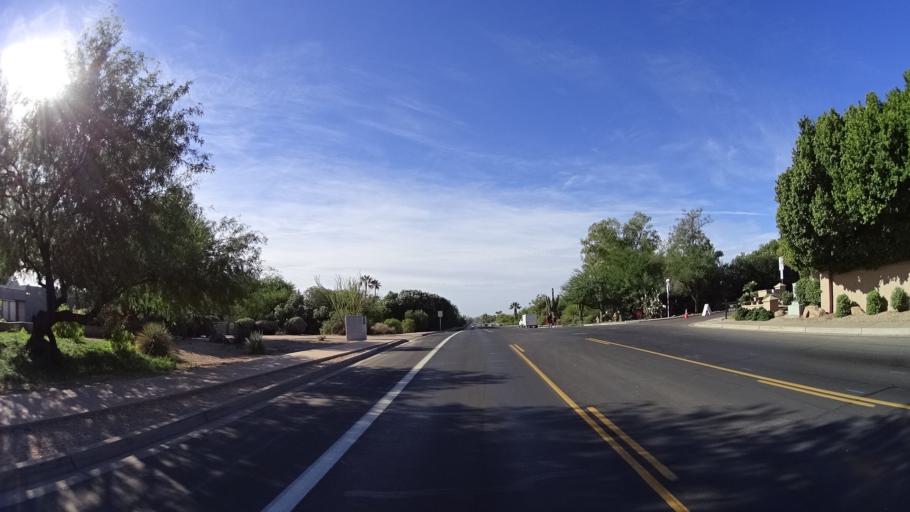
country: US
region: Arizona
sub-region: Maricopa County
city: Paradise Valley
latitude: 33.5133
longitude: -111.9432
